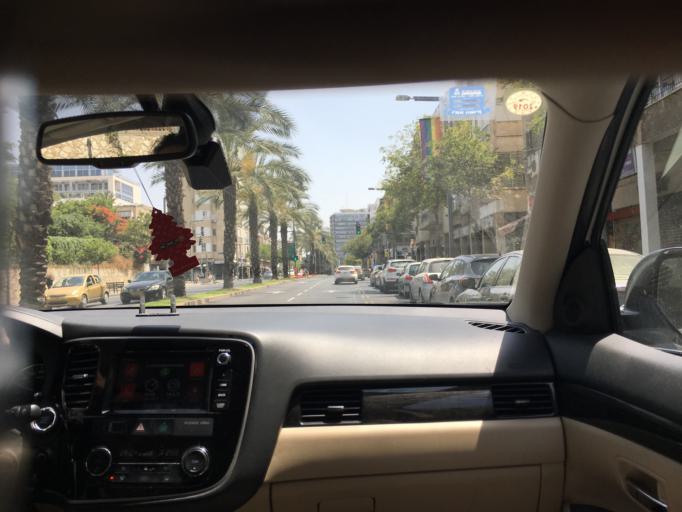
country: IL
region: Tel Aviv
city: Tel Aviv
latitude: 32.0860
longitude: 34.7817
